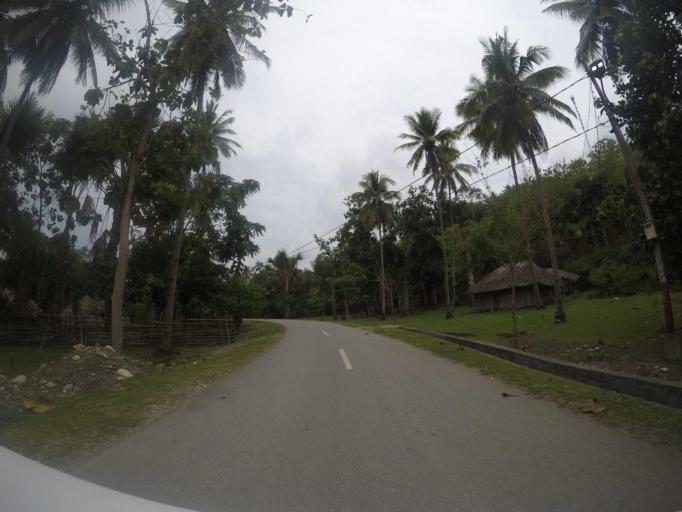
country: TL
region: Viqueque
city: Viqueque
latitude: -8.8628
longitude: 126.3670
